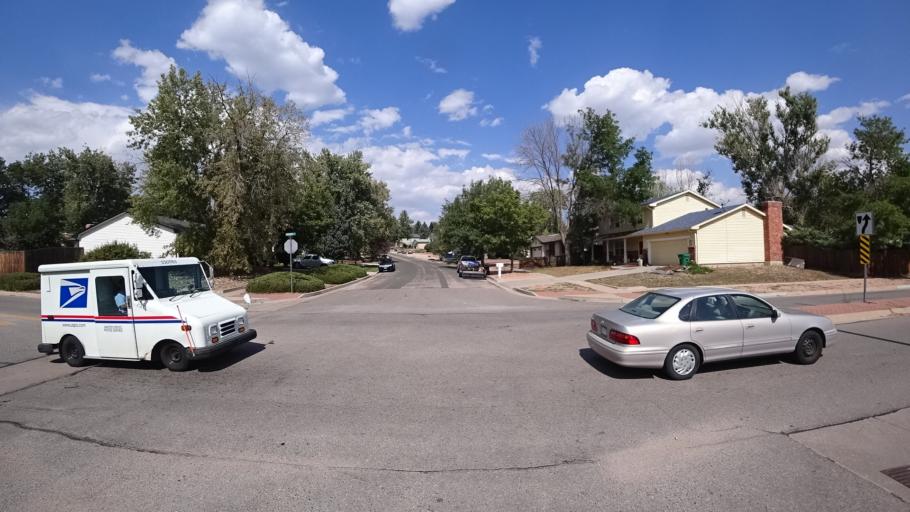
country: US
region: Colorado
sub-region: El Paso County
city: Colorado Springs
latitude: 38.8512
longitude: -104.7638
